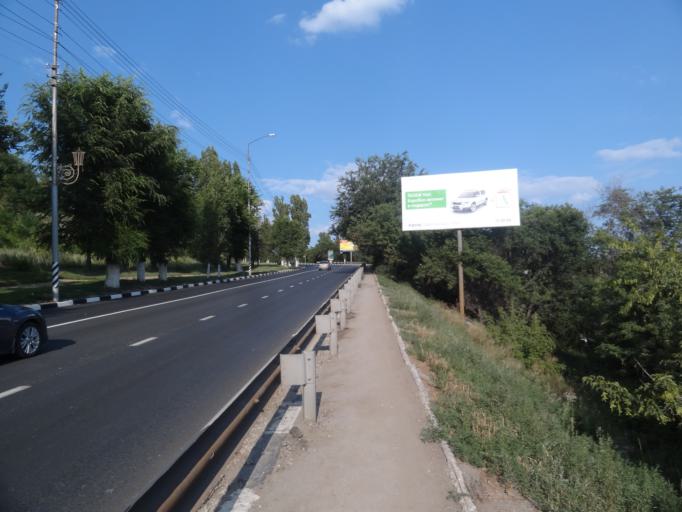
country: RU
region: Saratov
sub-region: Saratovskiy Rayon
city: Saratov
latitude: 51.5501
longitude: 46.0490
